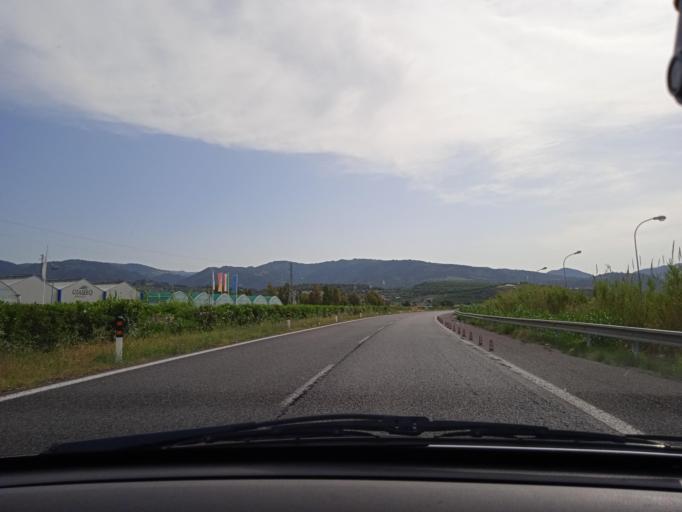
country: IT
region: Sicily
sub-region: Messina
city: Tonnarella
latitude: 38.1165
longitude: 15.1101
